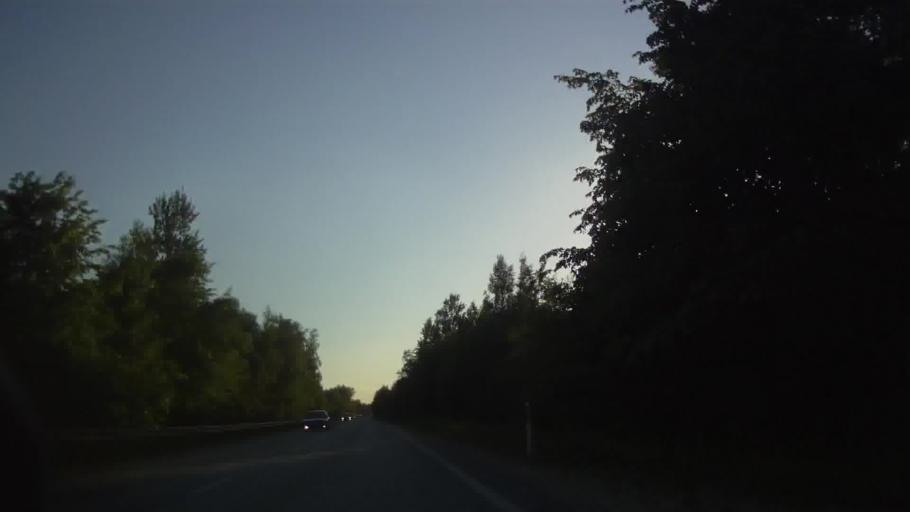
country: LV
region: Livani
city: Livani
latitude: 56.5291
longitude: 26.3869
